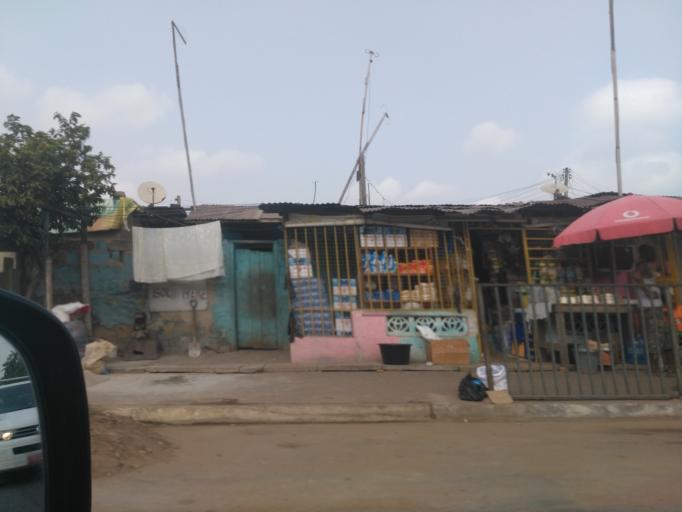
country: GH
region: Greater Accra
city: Accra
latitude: 5.5813
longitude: -0.1949
